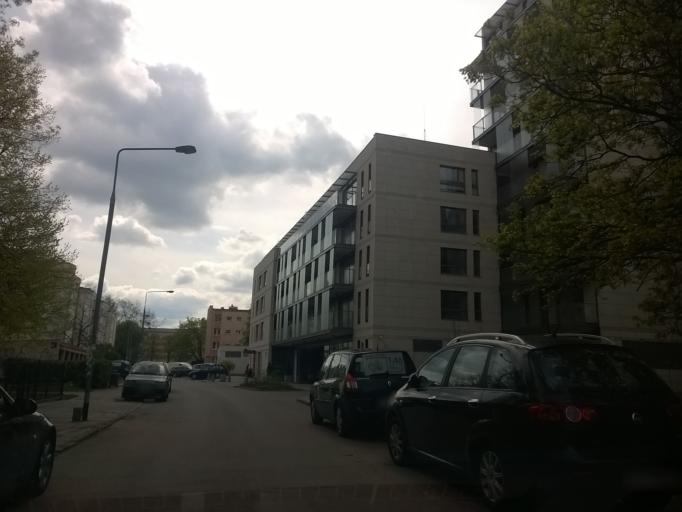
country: PL
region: Masovian Voivodeship
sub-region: Warszawa
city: Mokotow
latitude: 52.1908
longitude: 21.0124
